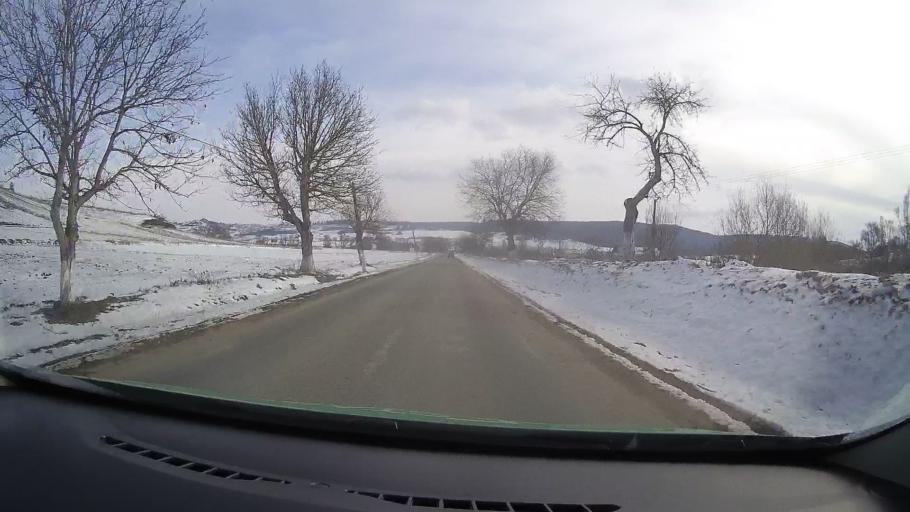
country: RO
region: Sibiu
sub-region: Comuna Iacobeni
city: Iacobeni
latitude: 46.0426
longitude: 24.7290
